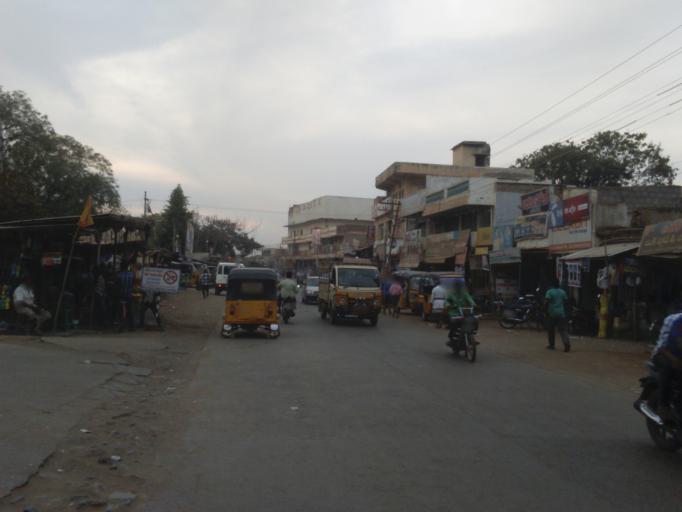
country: IN
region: Andhra Pradesh
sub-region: Kurnool
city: Nandikotkur
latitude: 15.8560
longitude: 78.2618
